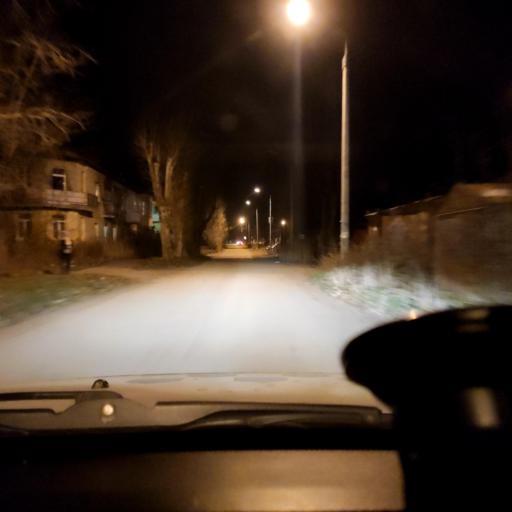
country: RU
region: Perm
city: Perm
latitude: 57.9696
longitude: 56.2226
